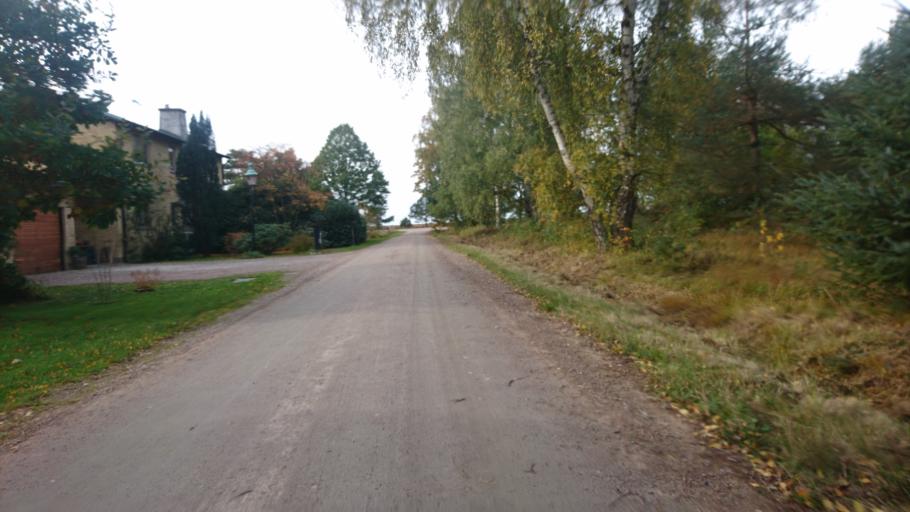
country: SE
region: Skane
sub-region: Vellinge Kommun
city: Ljunghusen
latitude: 55.4013
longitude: 12.9111
